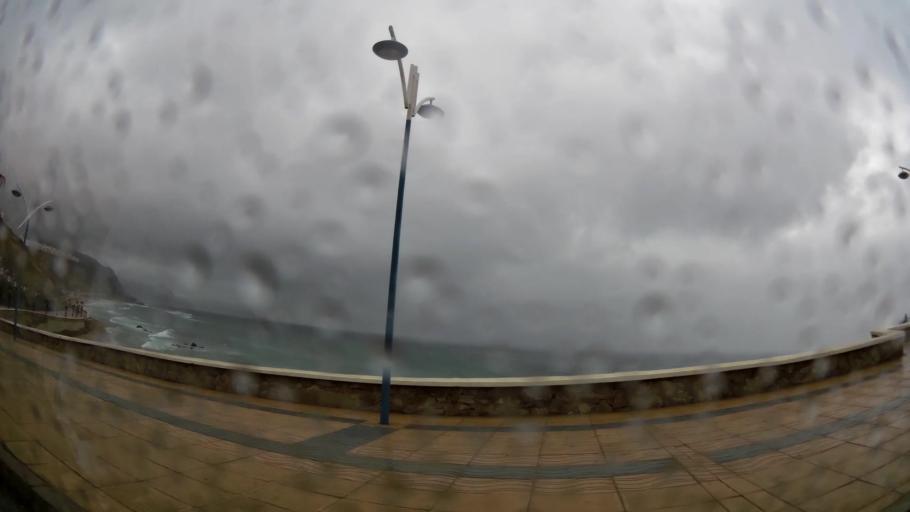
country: MA
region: Taza-Al Hoceima-Taounate
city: Al Hoceima
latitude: 35.2524
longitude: -3.9485
